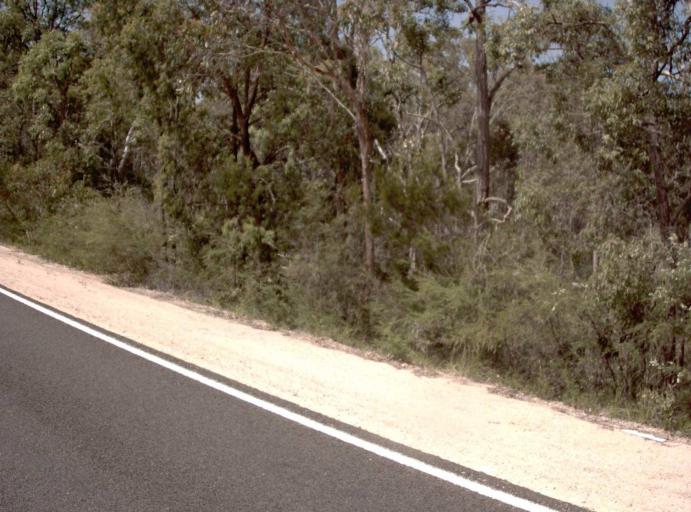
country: AU
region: New South Wales
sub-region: Bega Valley
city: Eden
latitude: -37.4319
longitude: 149.6449
